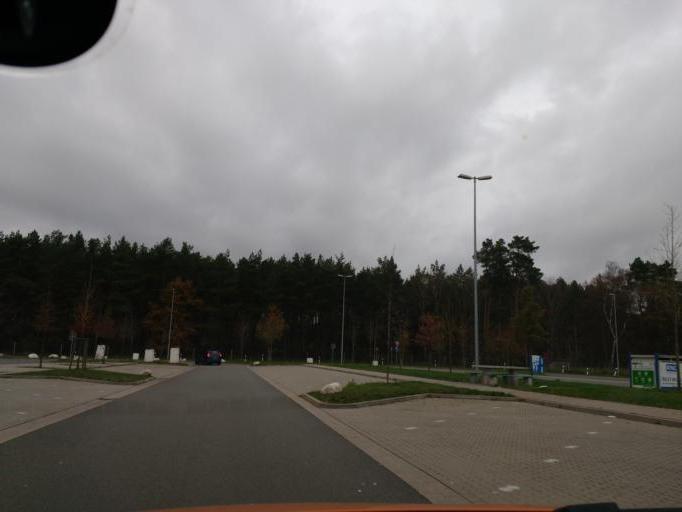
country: DE
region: Lower Saxony
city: Ottersberg
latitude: 53.0912
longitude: 9.1764
